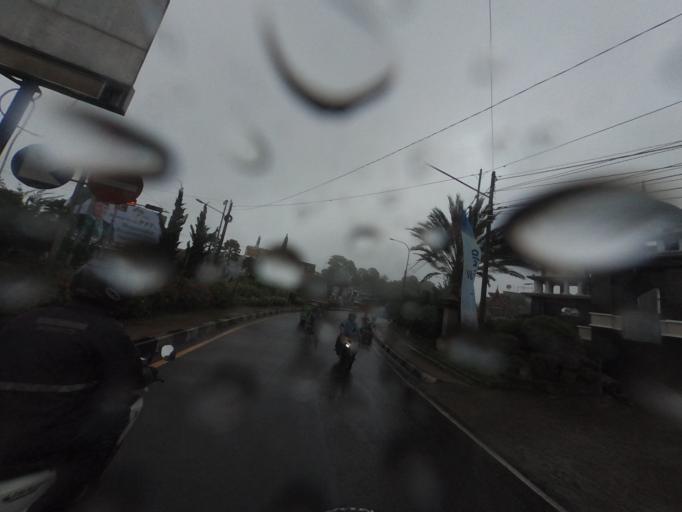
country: ID
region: West Java
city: Caringin
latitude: -6.6558
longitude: 106.8590
